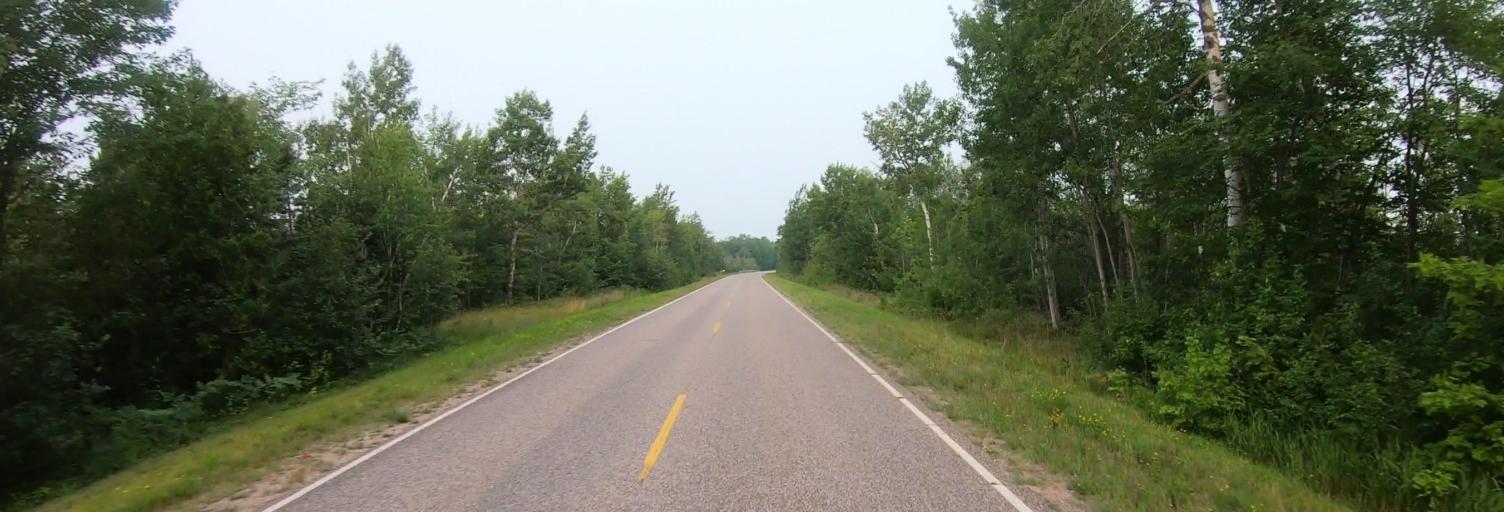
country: US
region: Michigan
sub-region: Chippewa County
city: Sault Ste. Marie
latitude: 46.4645
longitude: -84.8946
